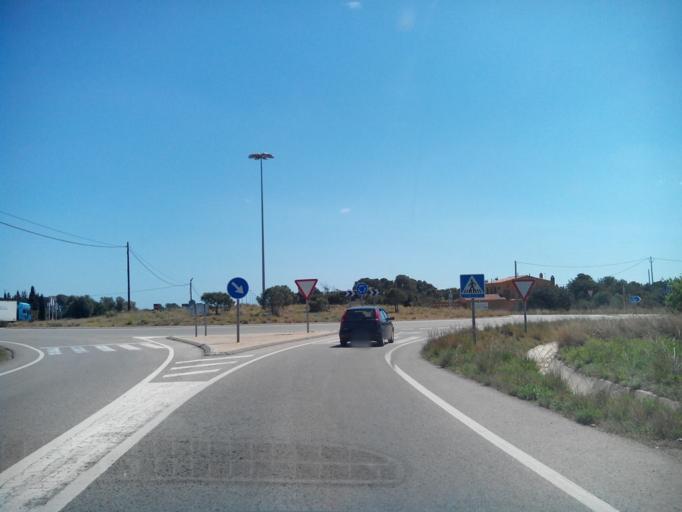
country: ES
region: Catalonia
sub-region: Provincia de Tarragona
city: Cambrils
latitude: 41.0574
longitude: 0.9941
